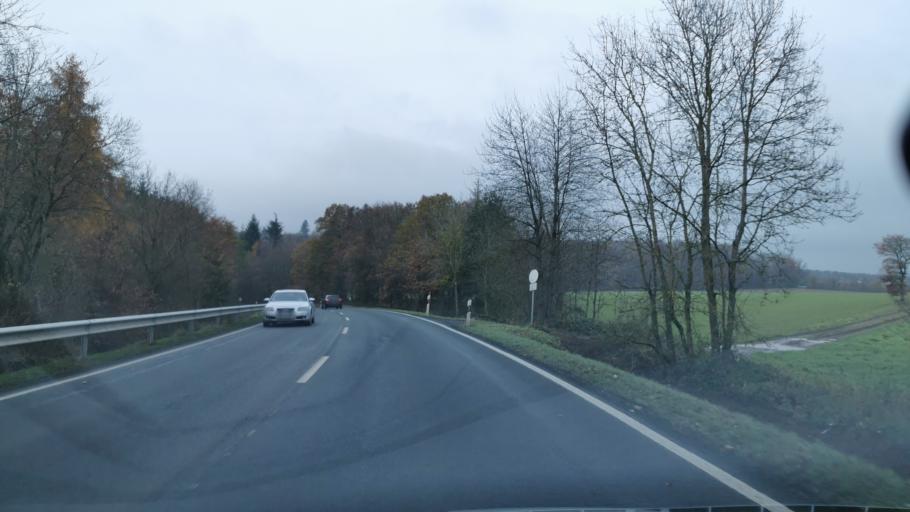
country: DE
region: Rheinland-Pfalz
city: Faid
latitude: 50.1586
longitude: 7.1102
